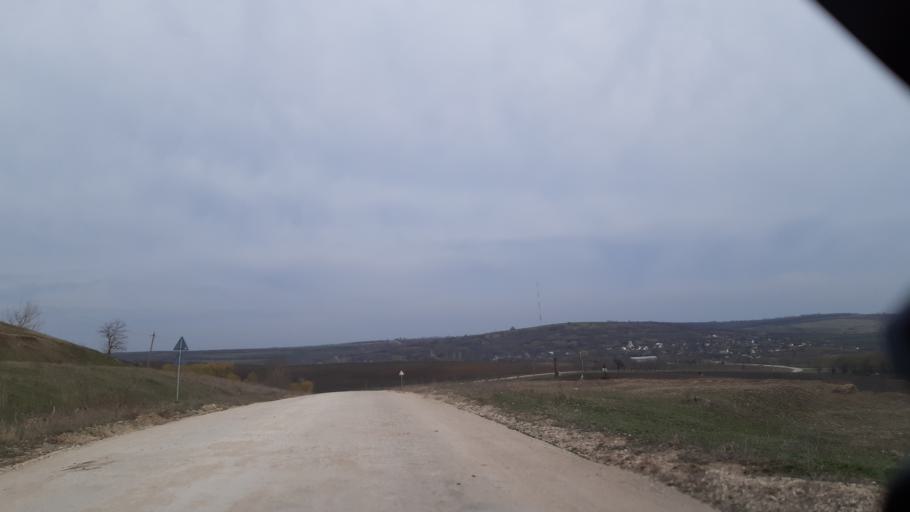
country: MD
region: Soldanesti
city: Soldanesti
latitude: 47.6800
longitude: 28.7840
